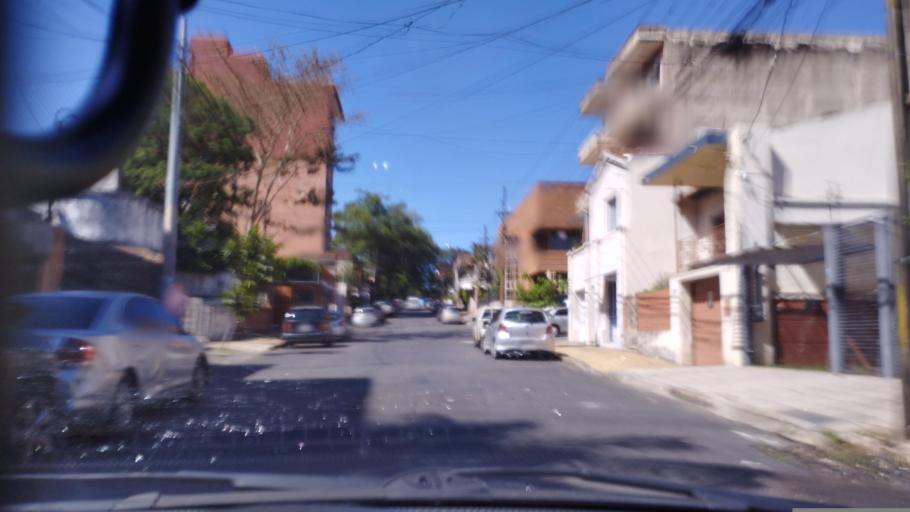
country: PY
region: Asuncion
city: Asuncion
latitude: -25.2889
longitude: -57.6434
